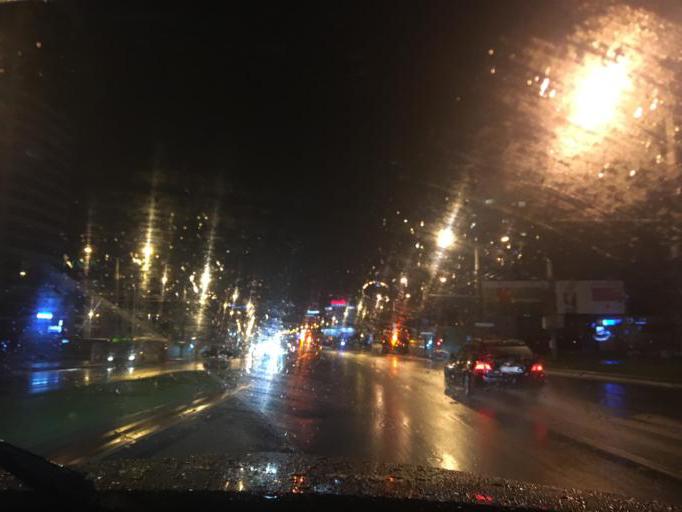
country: BY
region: Minsk
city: Minsk
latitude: 53.8883
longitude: 27.5194
